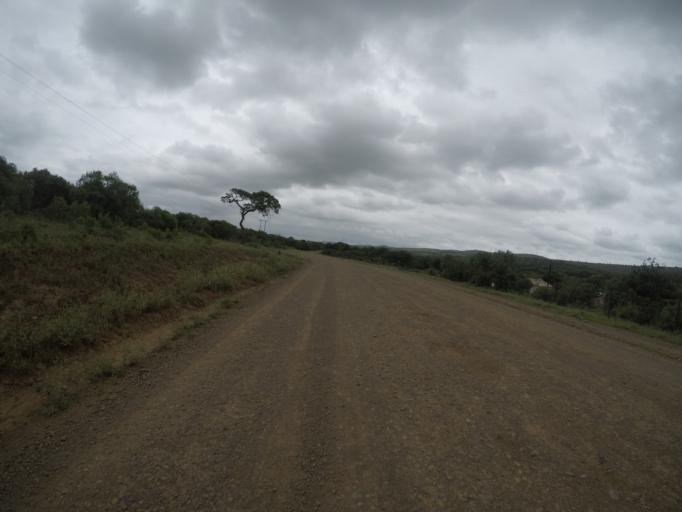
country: ZA
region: KwaZulu-Natal
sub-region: uThungulu District Municipality
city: Empangeni
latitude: -28.5929
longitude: 31.8374
